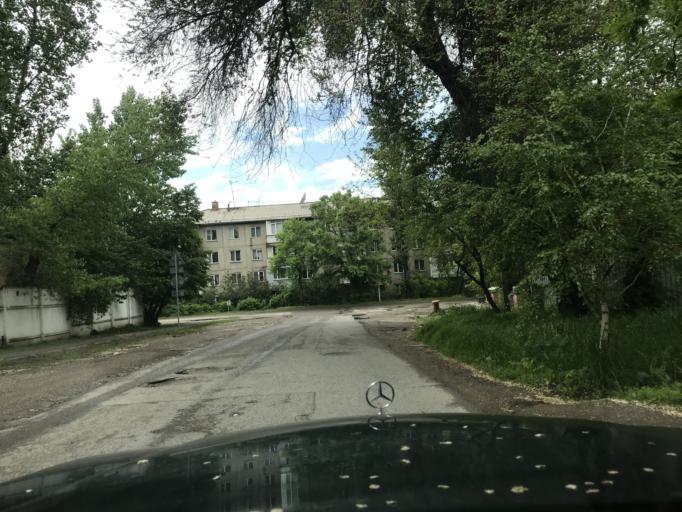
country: KZ
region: Almaty Qalasy
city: Almaty
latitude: 43.2079
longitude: 76.8692
